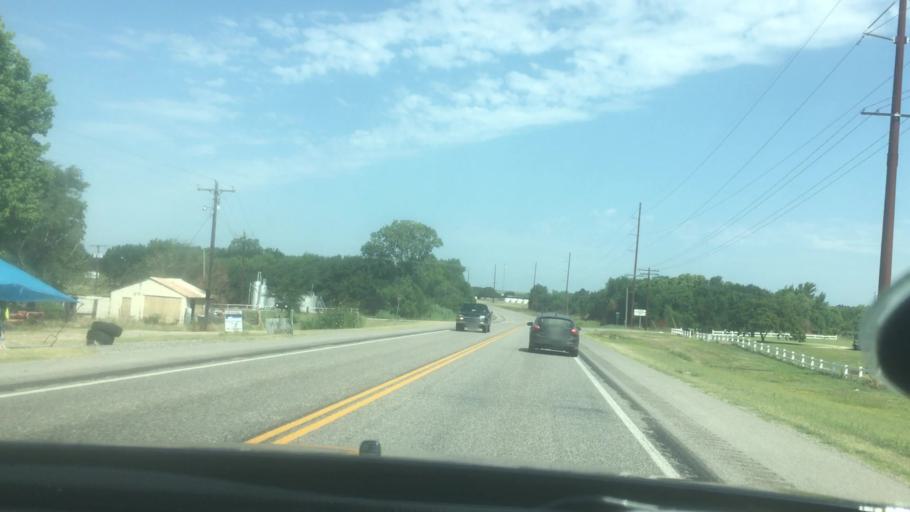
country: US
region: Oklahoma
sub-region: Seminole County
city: Konawa
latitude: 34.8608
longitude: -96.8240
